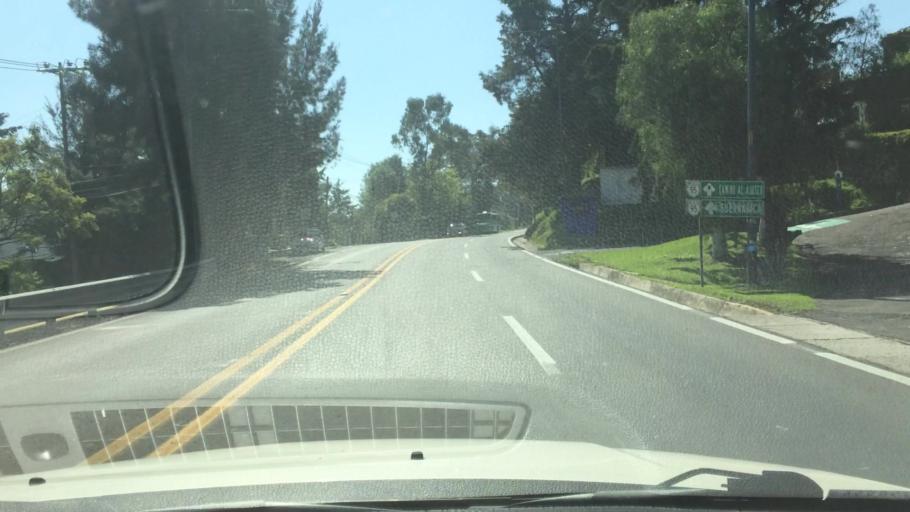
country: MX
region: Mexico City
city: Tlalpan
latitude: 19.2415
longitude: -99.1645
